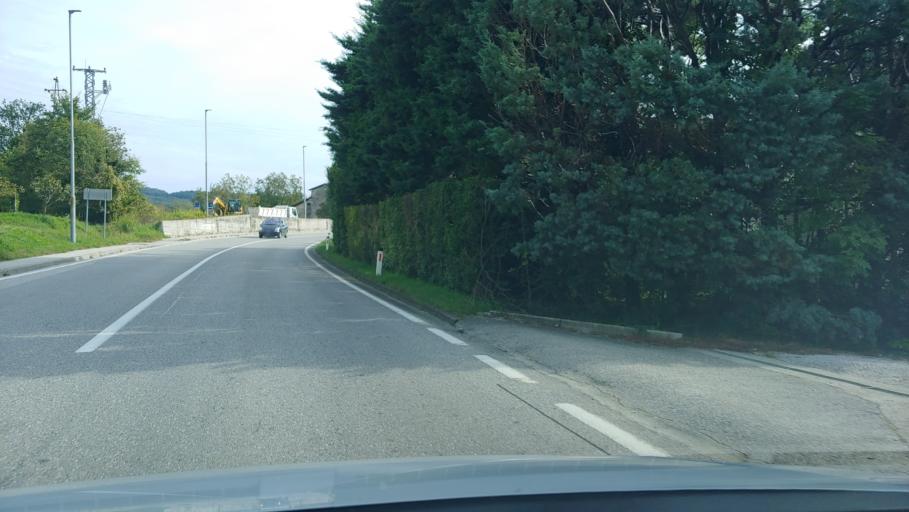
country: SI
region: Nova Gorica
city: Sempas
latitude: 45.9261
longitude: 13.7538
